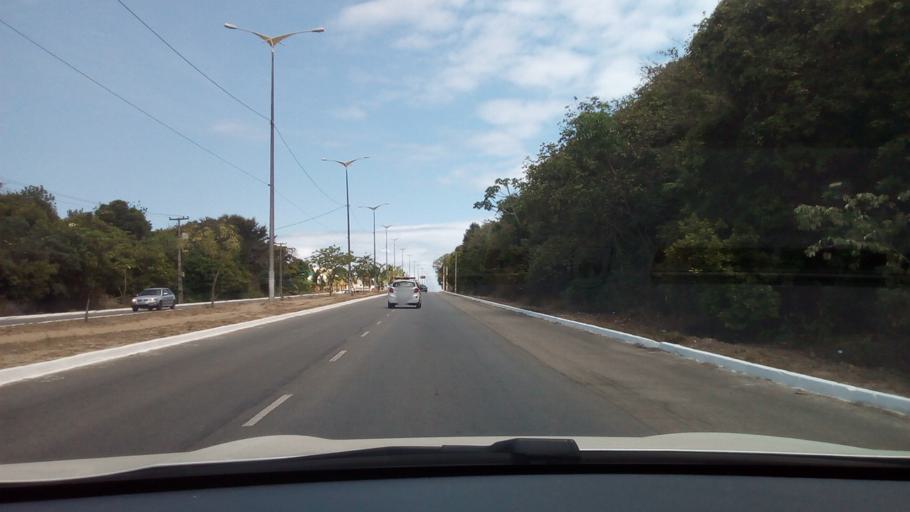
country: BR
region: Paraiba
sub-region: Joao Pessoa
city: Joao Pessoa
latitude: -7.1606
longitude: -34.8108
